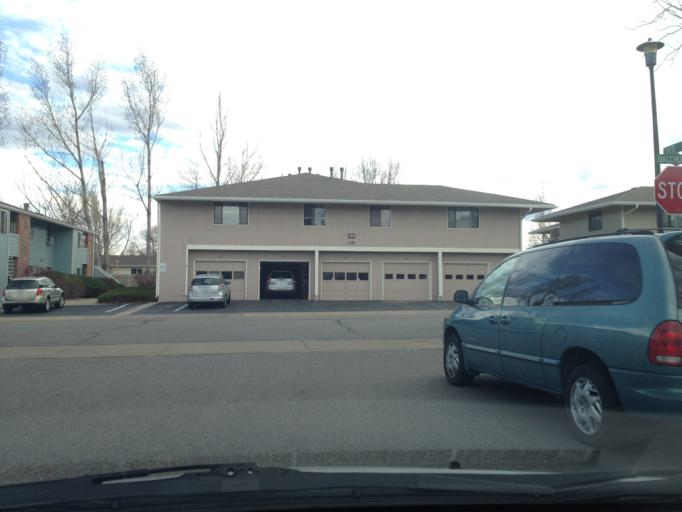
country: US
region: Colorado
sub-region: Boulder County
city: Lafayette
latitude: 39.9840
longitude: -105.1063
